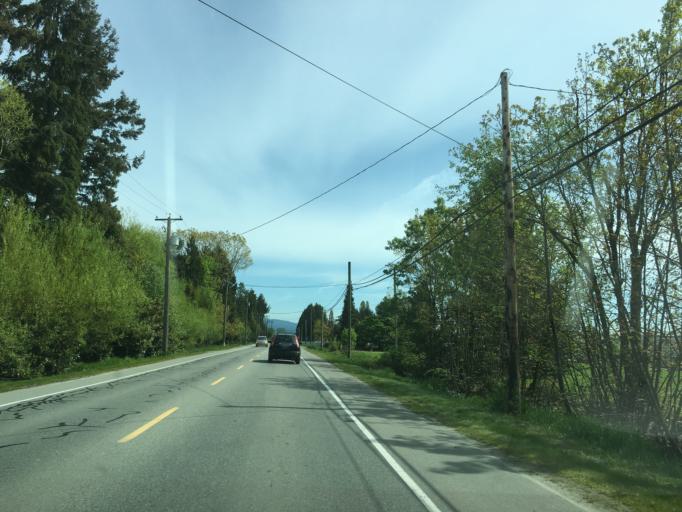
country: CA
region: British Columbia
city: Pitt Meadows
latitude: 49.2442
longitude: -122.6950
